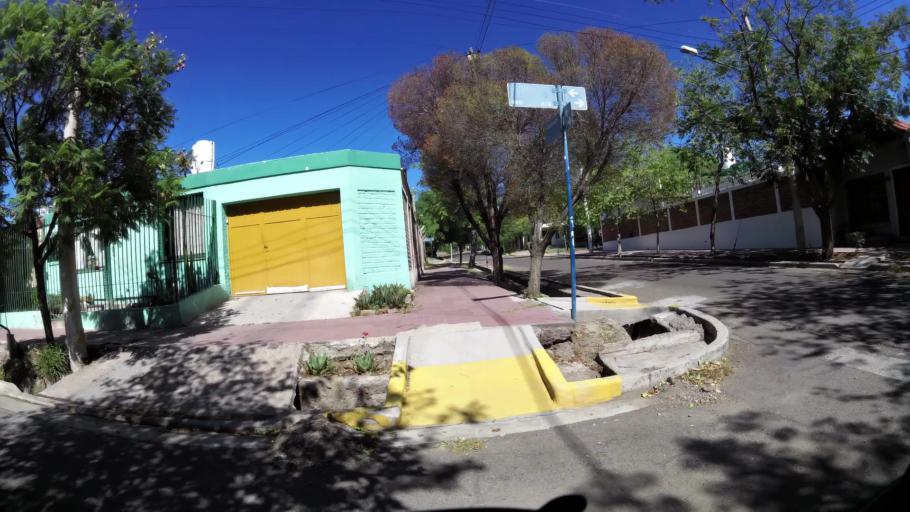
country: AR
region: Mendoza
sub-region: Departamento de Godoy Cruz
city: Godoy Cruz
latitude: -32.9177
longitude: -68.8784
